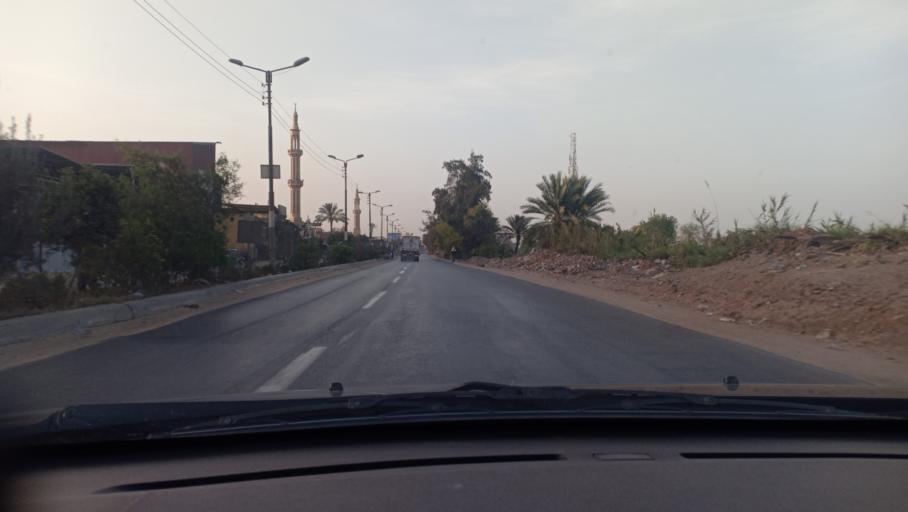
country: EG
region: Muhafazat al Gharbiyah
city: Zifta
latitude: 30.6447
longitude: 31.2825
